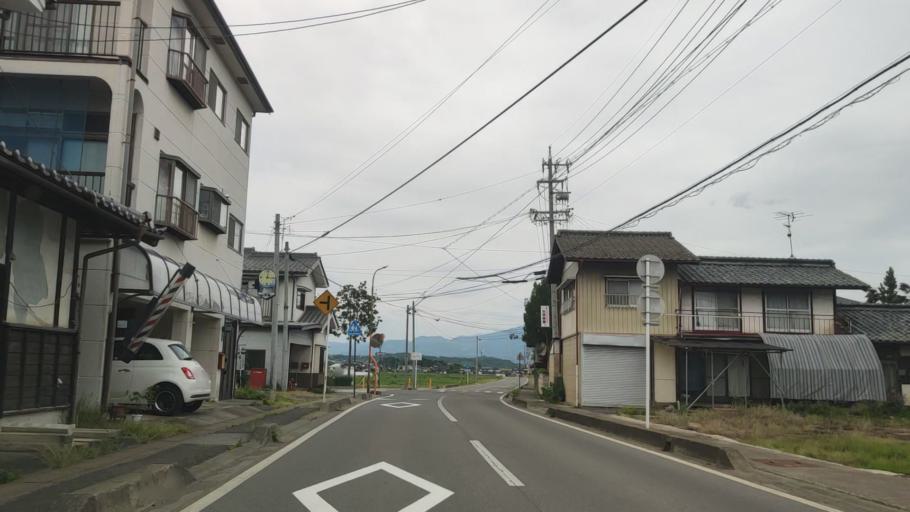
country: JP
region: Nagano
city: Kamimaruko
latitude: 36.2918
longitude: 138.3163
